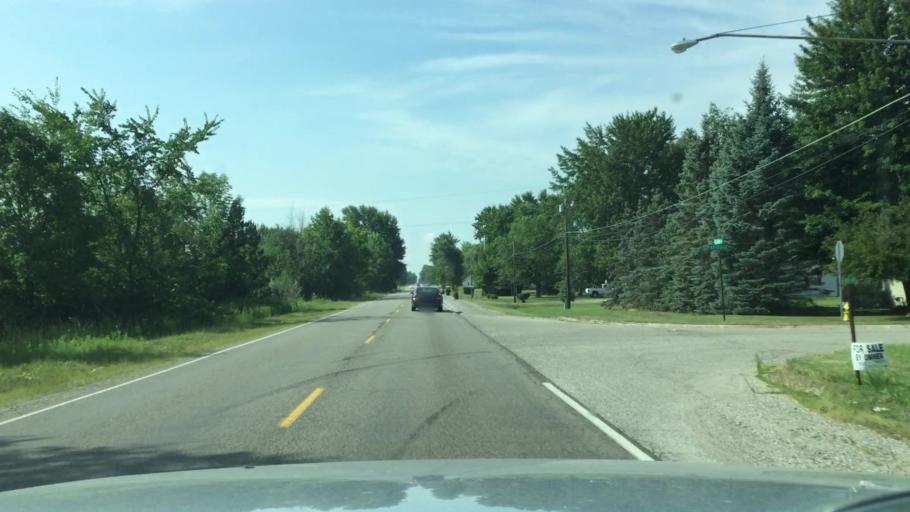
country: US
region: Michigan
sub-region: Genesee County
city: Flushing
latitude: 43.1144
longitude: -83.8138
